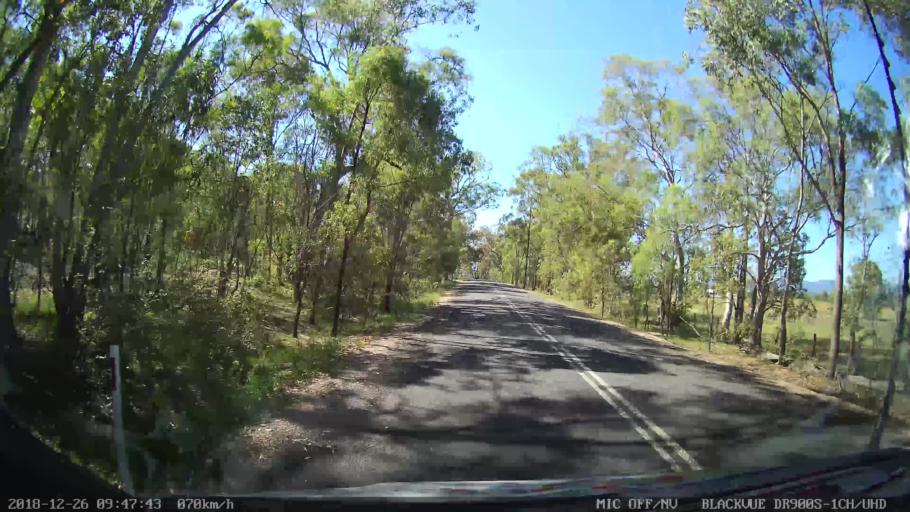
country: AU
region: New South Wales
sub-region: Mid-Western Regional
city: Kandos
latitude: -32.9818
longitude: 150.1079
